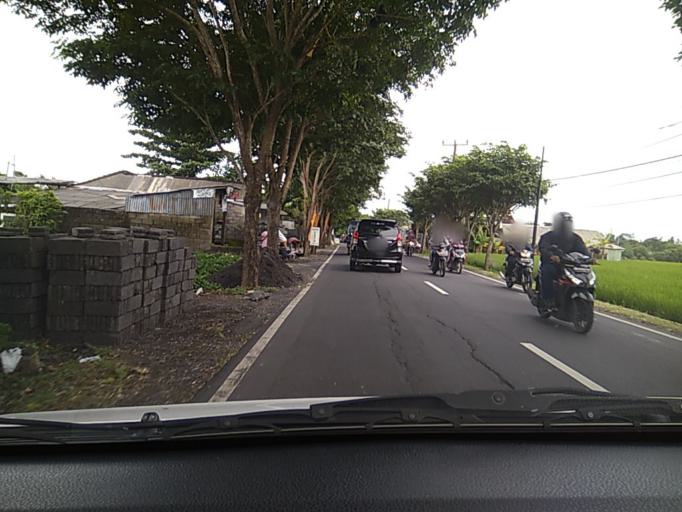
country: ID
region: Bali
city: Banjar Kerobokan
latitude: -8.6290
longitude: 115.1306
